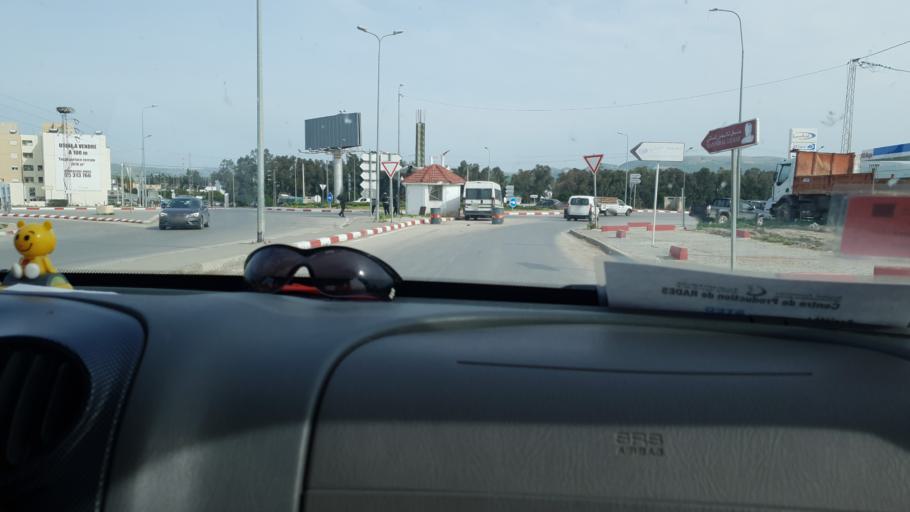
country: TN
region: Bajah
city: Beja
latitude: 36.7293
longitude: 9.2065
